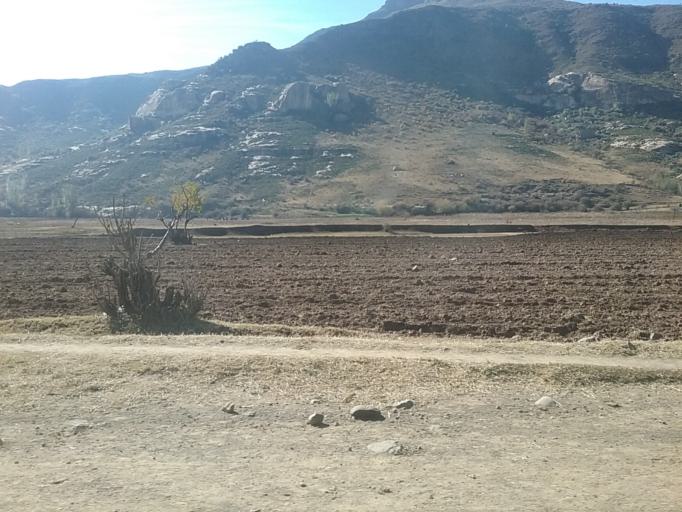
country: LS
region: Berea
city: Teyateyaneng
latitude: -29.2487
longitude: 27.9091
